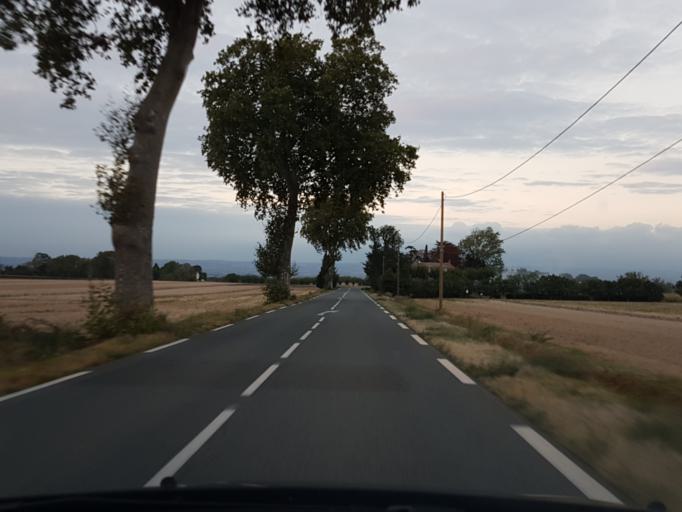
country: FR
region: Languedoc-Roussillon
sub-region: Departement de l'Aude
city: Bram
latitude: 43.2006
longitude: 2.0592
